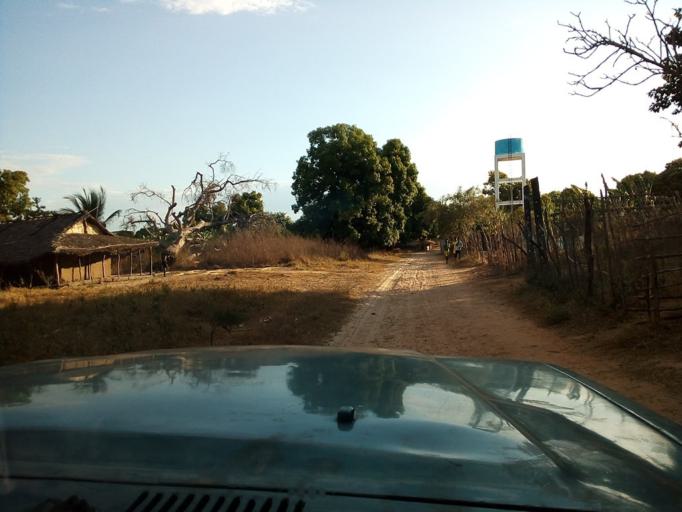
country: MG
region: Boeny
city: Sitampiky
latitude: -16.1243
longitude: 45.5124
